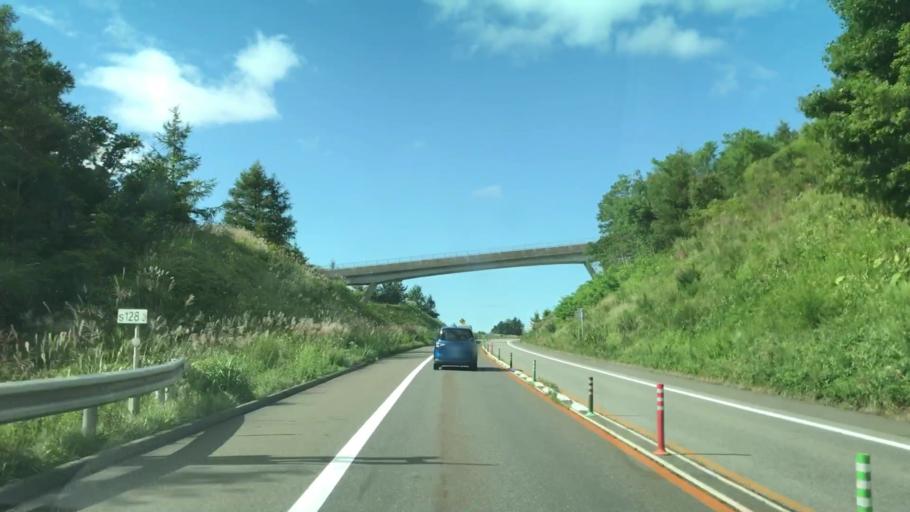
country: JP
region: Hokkaido
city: Date
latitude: 42.4450
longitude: 140.9148
